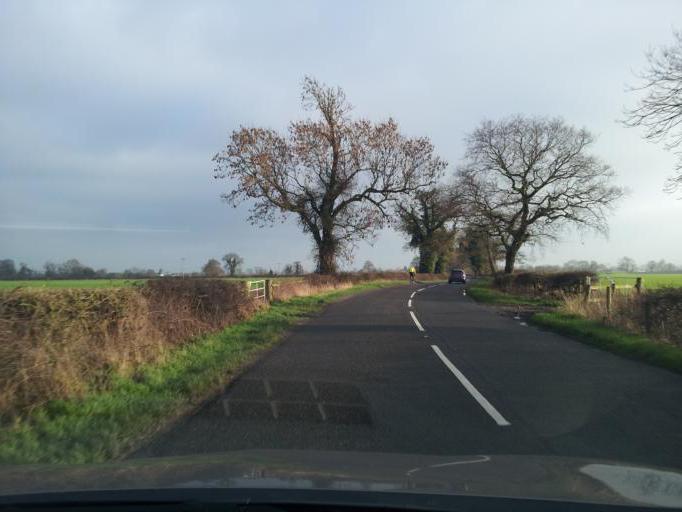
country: GB
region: England
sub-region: Derbyshire
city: Rodsley
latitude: 52.8736
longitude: -1.7300
